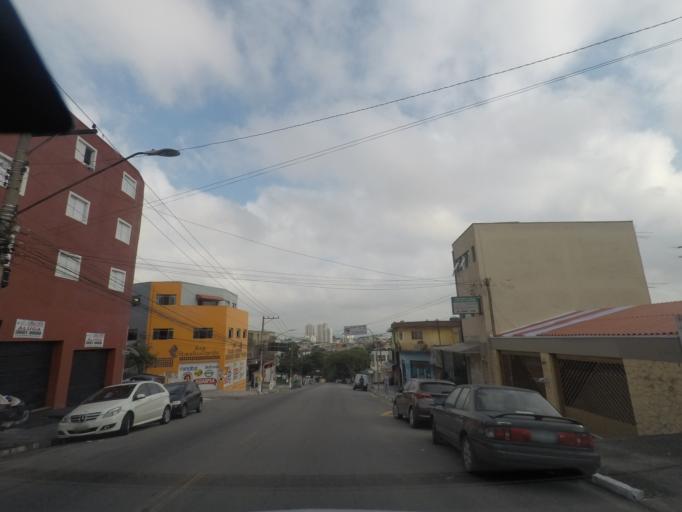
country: BR
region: Sao Paulo
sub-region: Osasco
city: Osasco
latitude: -23.5696
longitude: -46.7789
